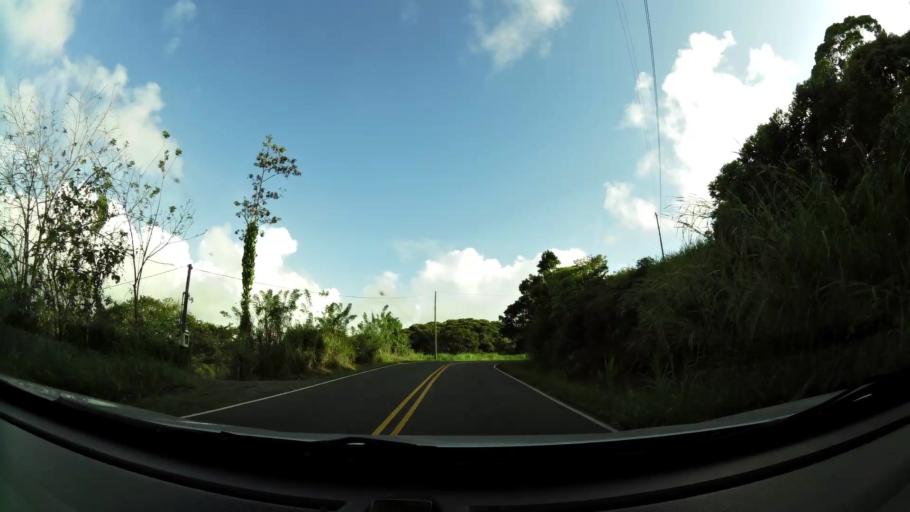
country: CR
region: Limon
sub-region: Canton de Siquirres
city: Siquirres
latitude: 10.0578
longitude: -83.5534
